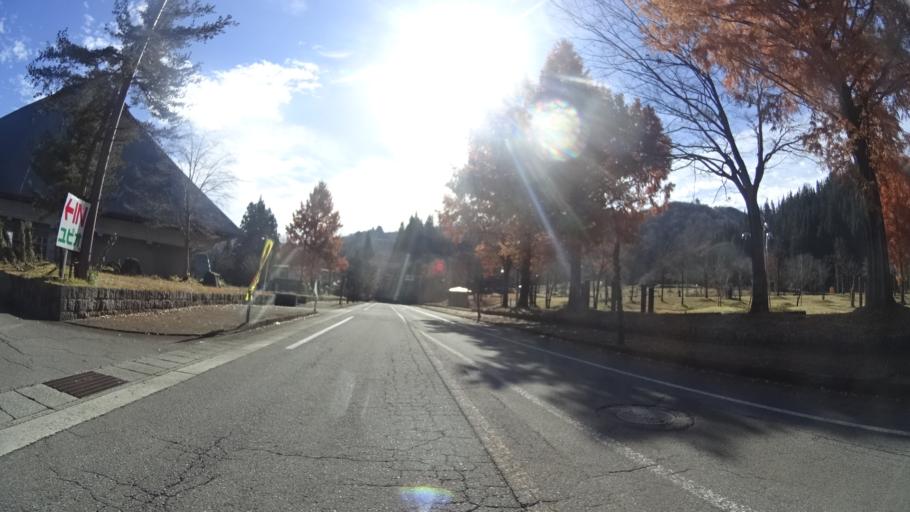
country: JP
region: Niigata
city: Muikamachi
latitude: 37.1978
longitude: 139.0771
